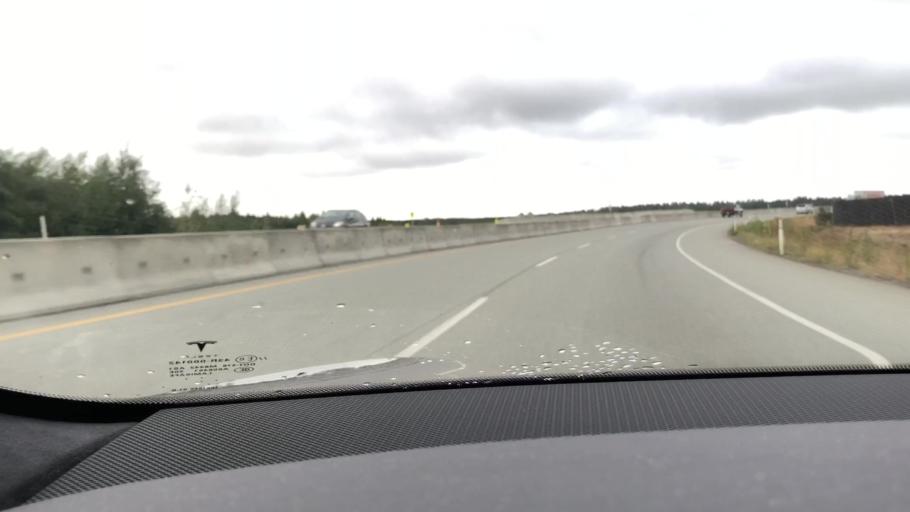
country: CA
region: British Columbia
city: Ladner
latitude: 49.1296
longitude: -123.0130
